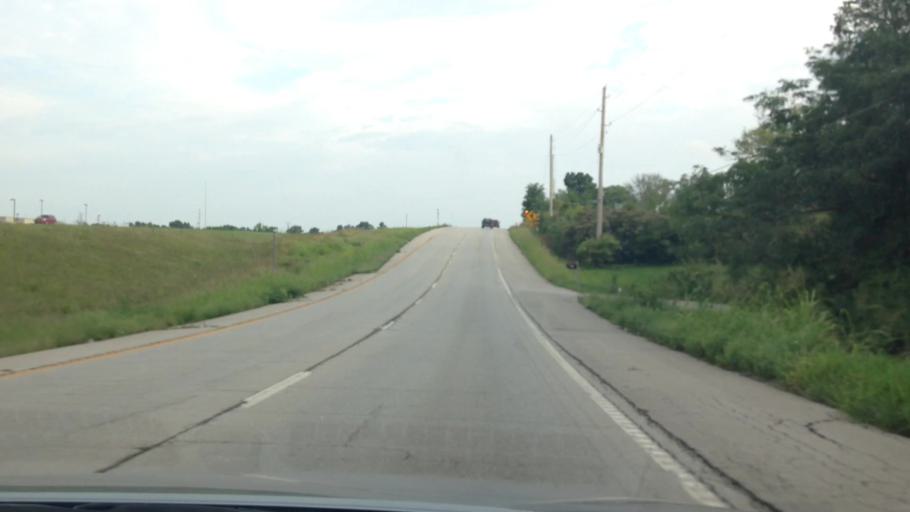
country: US
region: Missouri
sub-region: Clay County
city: Smithville
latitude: 39.3504
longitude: -94.5839
